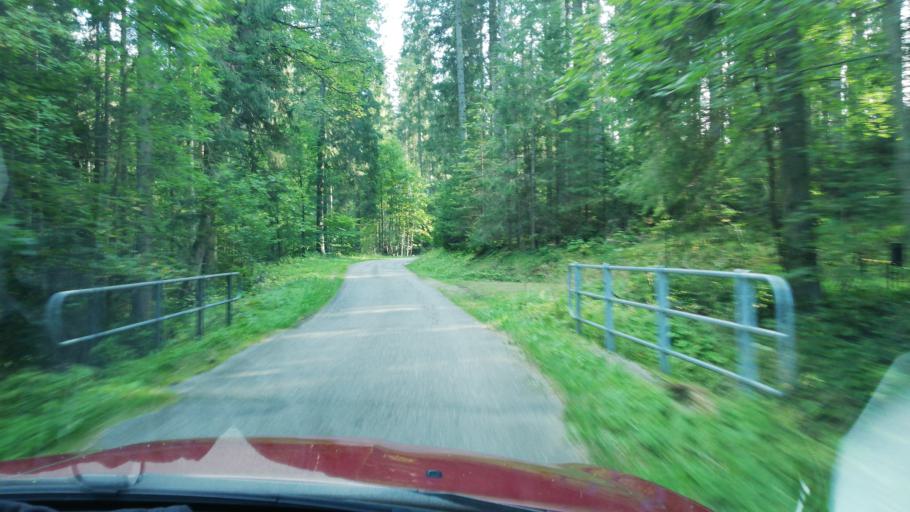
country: AT
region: Lower Austria
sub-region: Politischer Bezirk Zwettl
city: Langschlag
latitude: 48.4780
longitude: 14.8403
